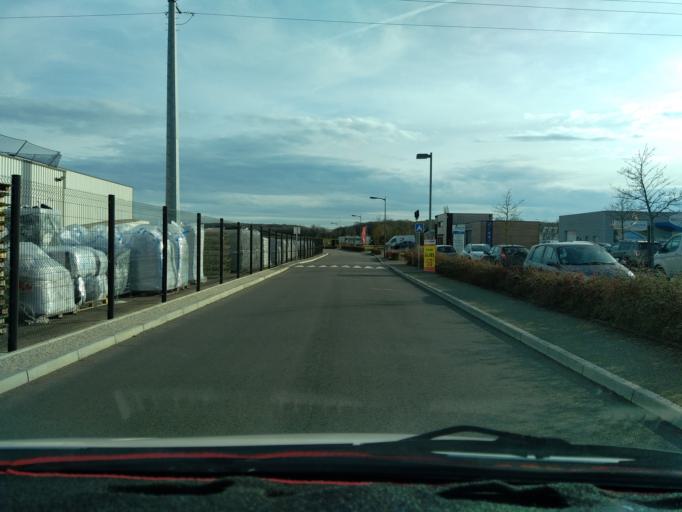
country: FR
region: Franche-Comte
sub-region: Departement de la Haute-Saone
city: Gray
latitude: 47.4345
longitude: 5.6025
